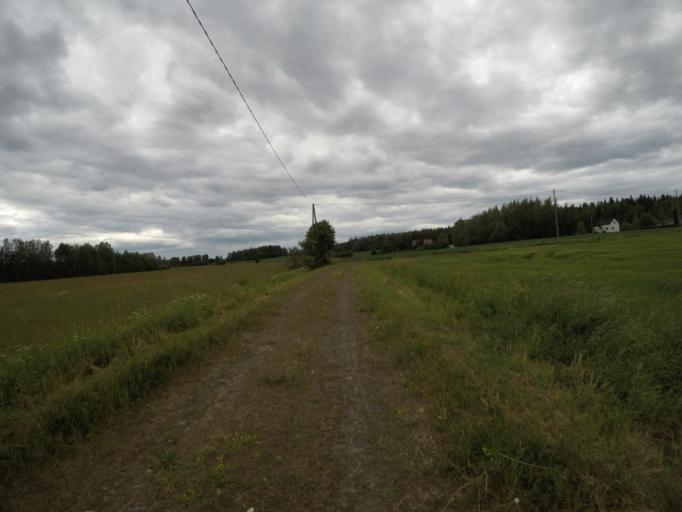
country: FI
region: Haeme
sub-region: Haemeenlinna
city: Haemeenlinna
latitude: 60.9725
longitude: 24.4578
